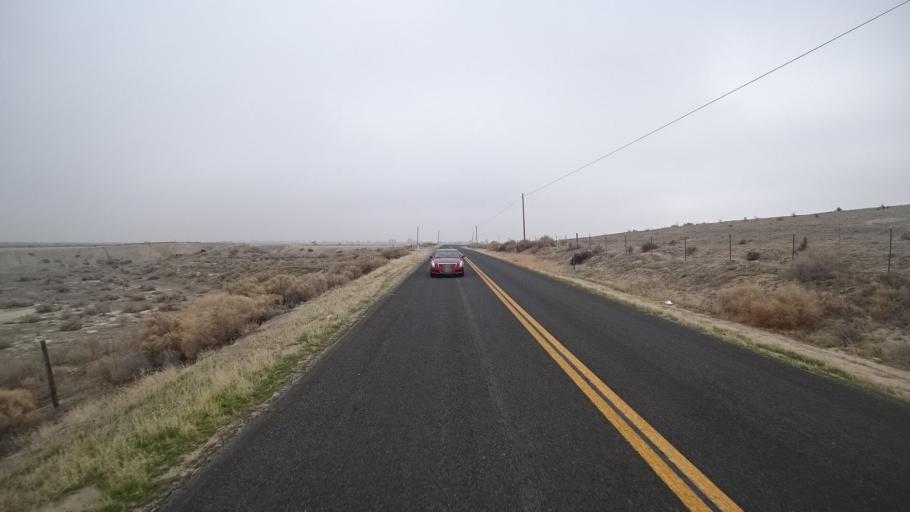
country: US
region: California
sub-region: Kern County
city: Ford City
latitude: 35.2501
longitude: -119.3037
